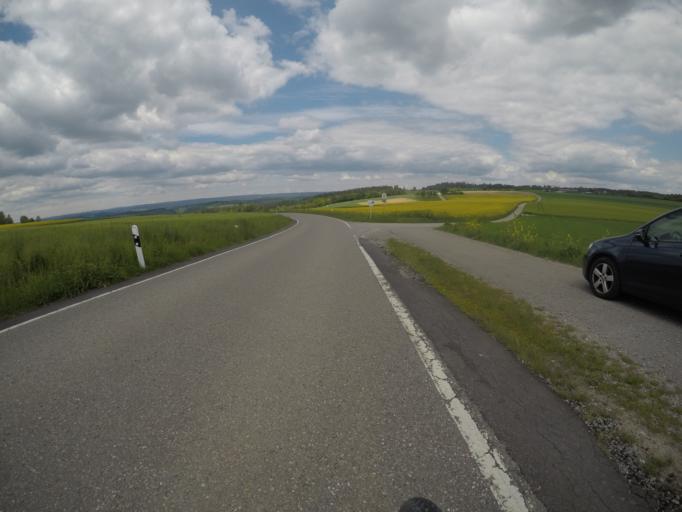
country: DE
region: Baden-Wuerttemberg
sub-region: Regierungsbezirk Stuttgart
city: Oberjettingen
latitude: 48.5830
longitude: 8.7554
